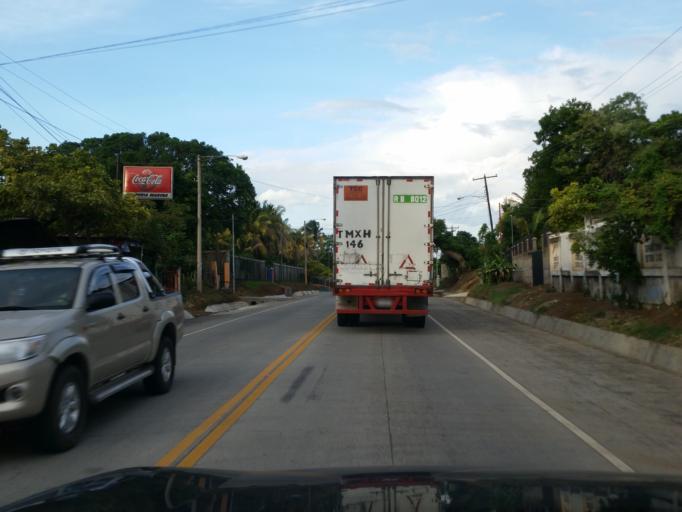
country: NI
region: Managua
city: Ciudad Sandino
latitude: 12.0998
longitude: -86.3437
